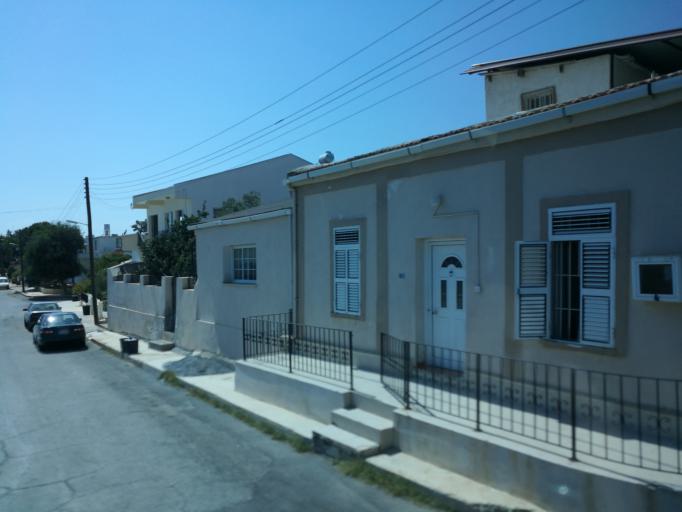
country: CY
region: Ammochostos
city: Famagusta
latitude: 35.1091
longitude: 33.9474
